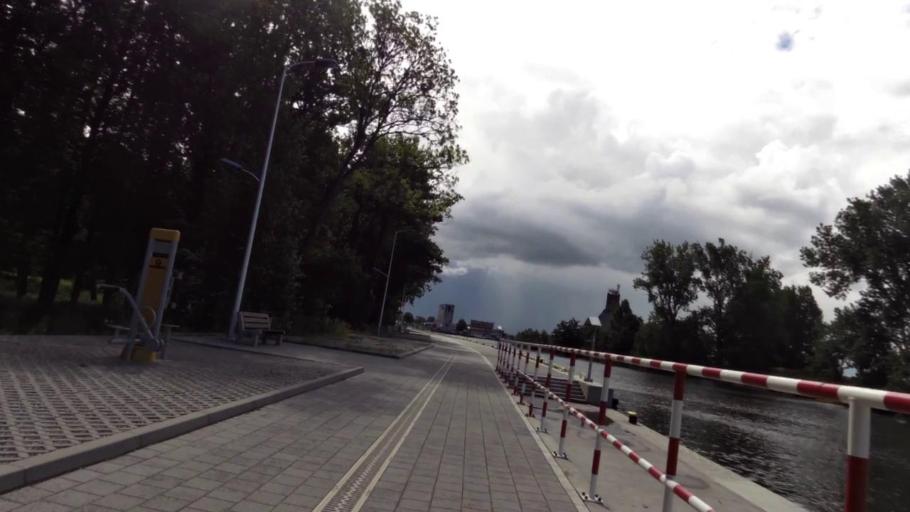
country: PL
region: West Pomeranian Voivodeship
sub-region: Powiat slawienski
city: Darlowo
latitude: 54.4297
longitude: 16.3934
